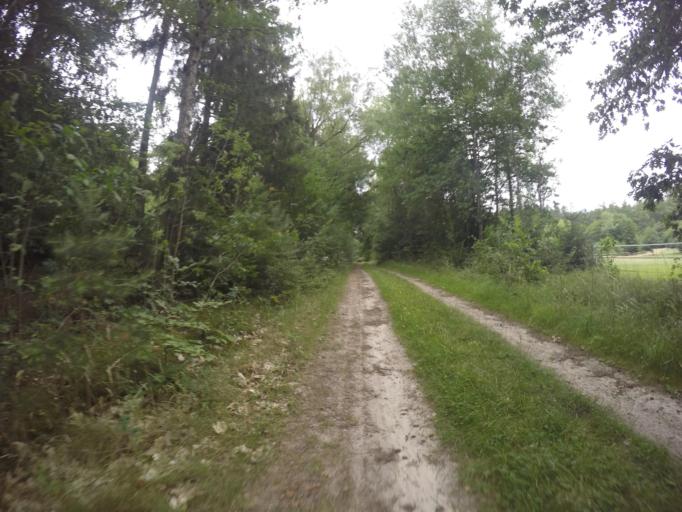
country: DE
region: Lower Saxony
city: Thomasburg
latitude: 53.2381
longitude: 10.6996
